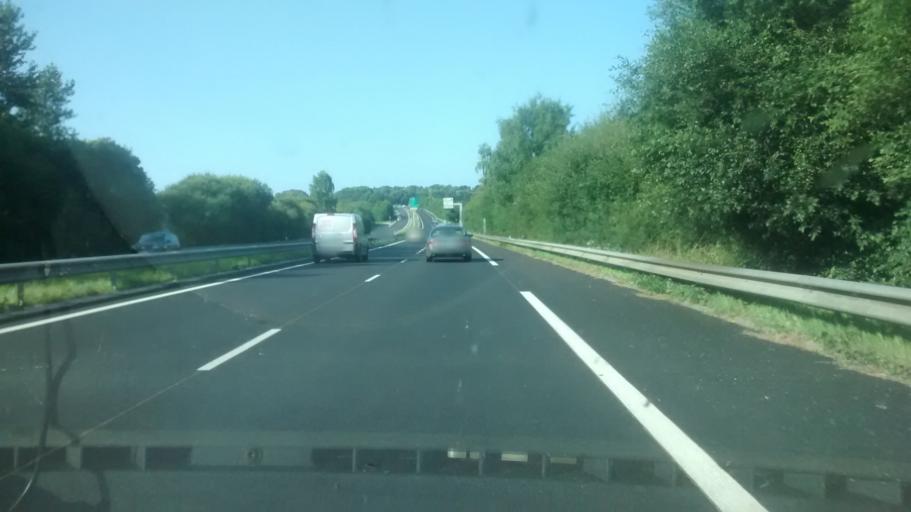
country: FR
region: Brittany
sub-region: Departement des Cotes-d'Armor
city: Saint-Samson-sur-Rance
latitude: 48.4768
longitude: -2.0460
